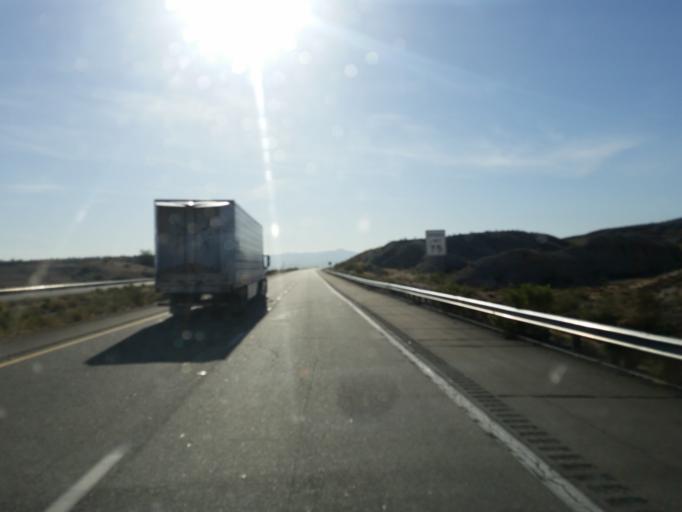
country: US
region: Arizona
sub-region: Mohave County
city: Desert Hills
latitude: 34.7257
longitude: -114.4038
